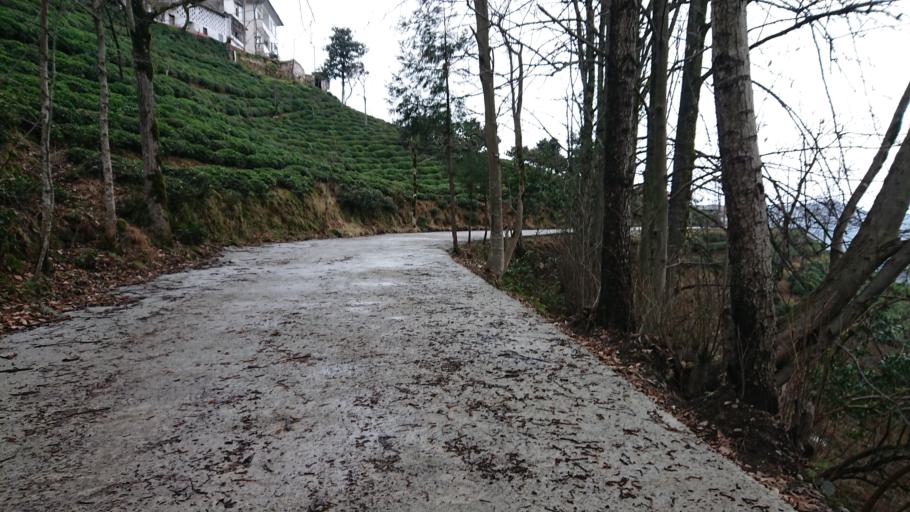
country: TR
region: Rize
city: Rize
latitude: 40.9773
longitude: 40.4942
